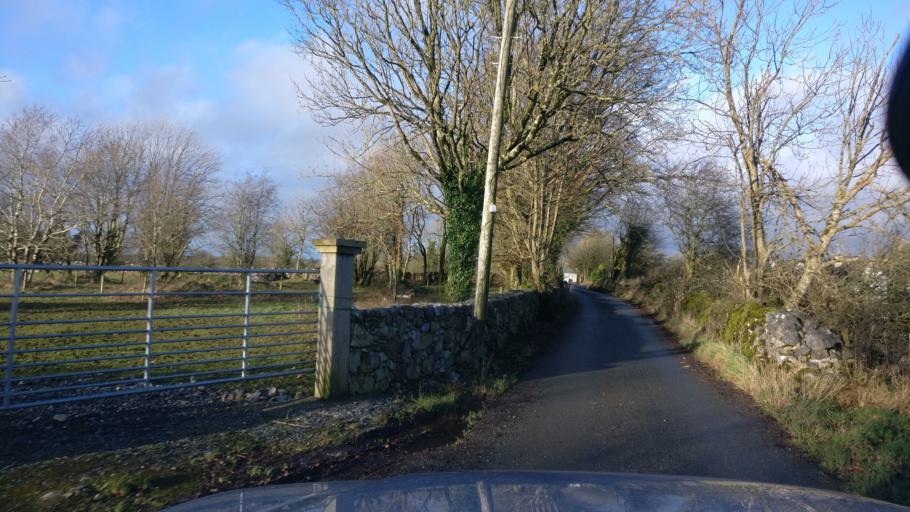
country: IE
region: Connaught
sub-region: County Galway
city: Loughrea
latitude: 53.2359
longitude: -8.5766
